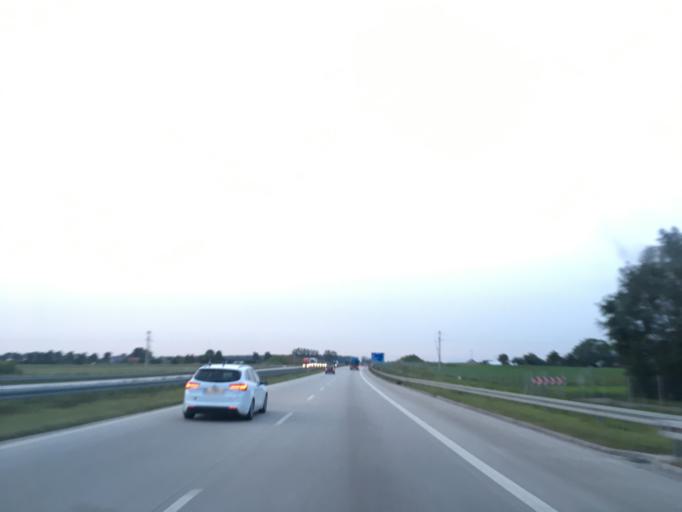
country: PL
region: Lodz Voivodeship
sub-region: Powiat zgierski
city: Strykow
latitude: 51.8754
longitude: 19.6496
